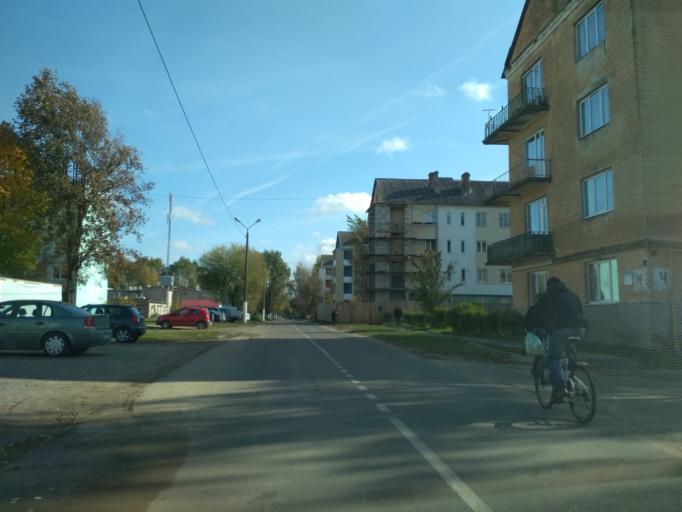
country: BY
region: Minsk
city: Mar''ina Horka
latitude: 53.5020
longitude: 28.1679
